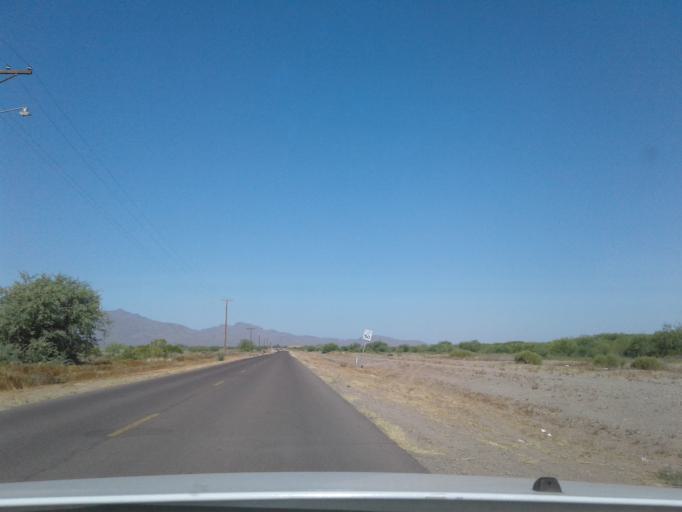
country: US
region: Arizona
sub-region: Maricopa County
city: Laveen
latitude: 33.3339
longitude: -112.1788
